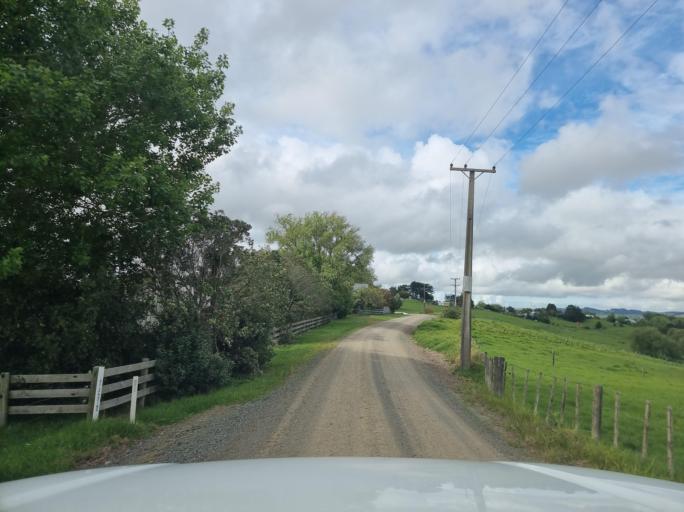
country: NZ
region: Northland
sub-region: Whangarei
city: Ruakaka
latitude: -36.1272
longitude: 174.2082
